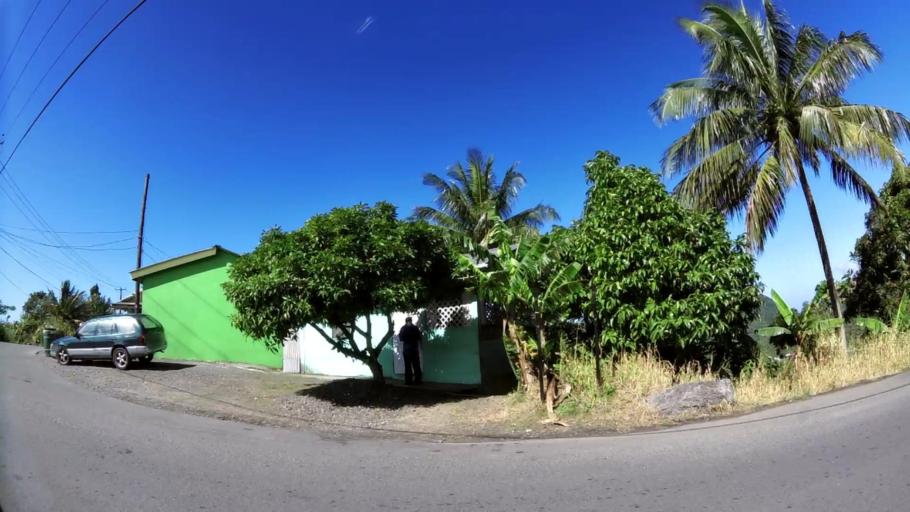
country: LC
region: Choiseul Quarter
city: Choiseul
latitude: 13.8131
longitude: -61.0411
